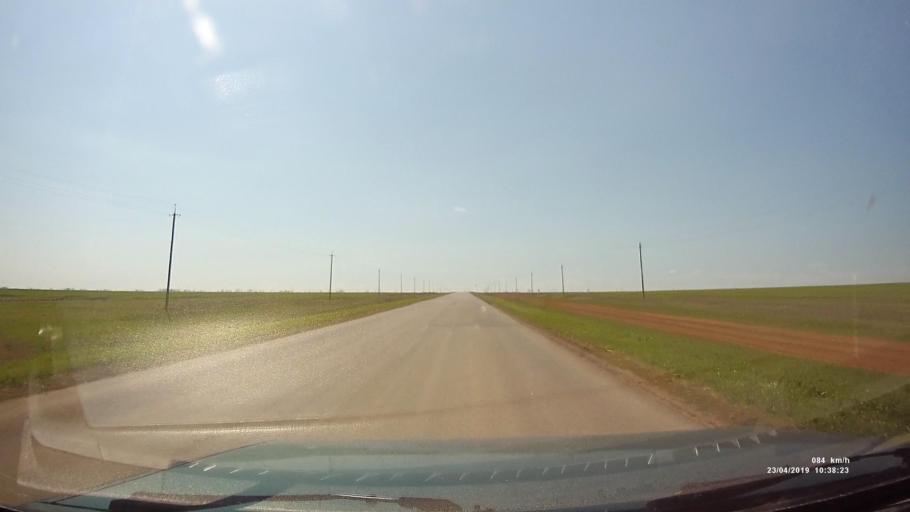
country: RU
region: Kalmykiya
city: Yashalta
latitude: 46.5335
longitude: 42.6388
